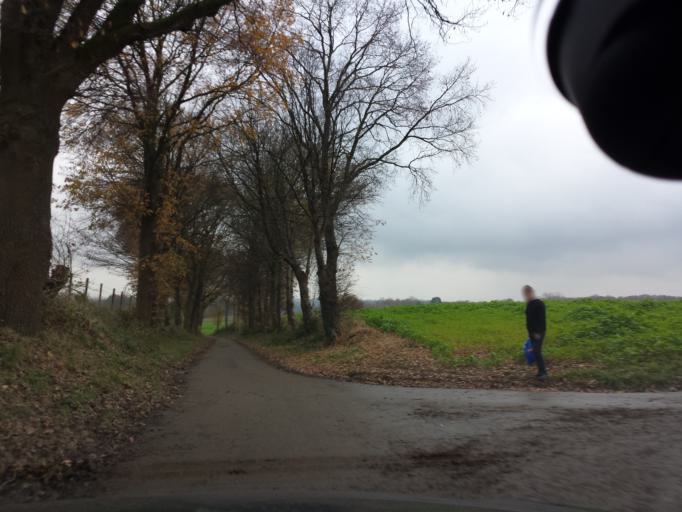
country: NL
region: Limburg
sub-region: Gemeente Kerkrade
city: Kerkrade
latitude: 50.9055
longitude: 6.0511
